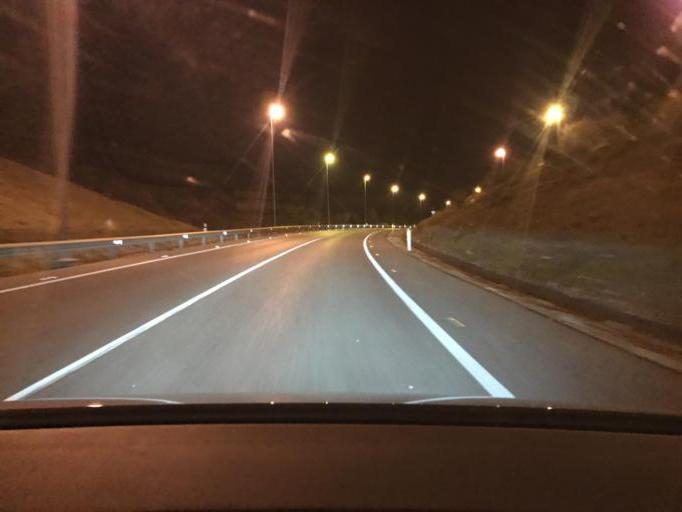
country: ES
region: Andalusia
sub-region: Provincia de Jaen
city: Jaen
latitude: 37.7817
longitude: -3.7554
